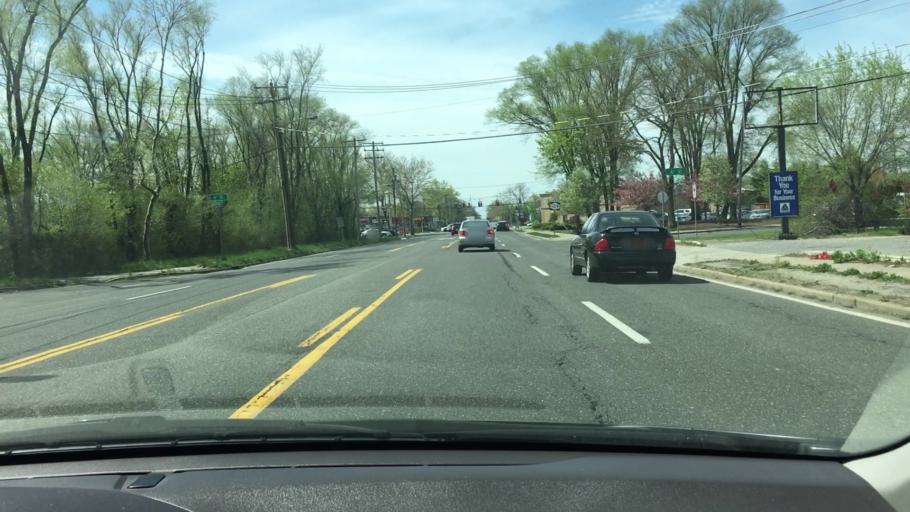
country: US
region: New York
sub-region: Suffolk County
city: North Lindenhurst
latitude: 40.7161
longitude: -73.3806
